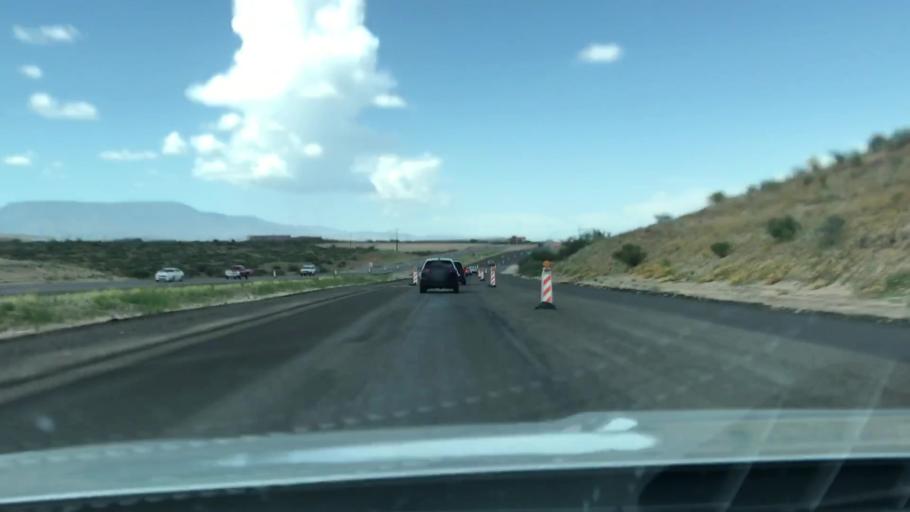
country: US
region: Arizona
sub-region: Yavapai County
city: Camp Verde
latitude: 34.6042
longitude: -111.9074
